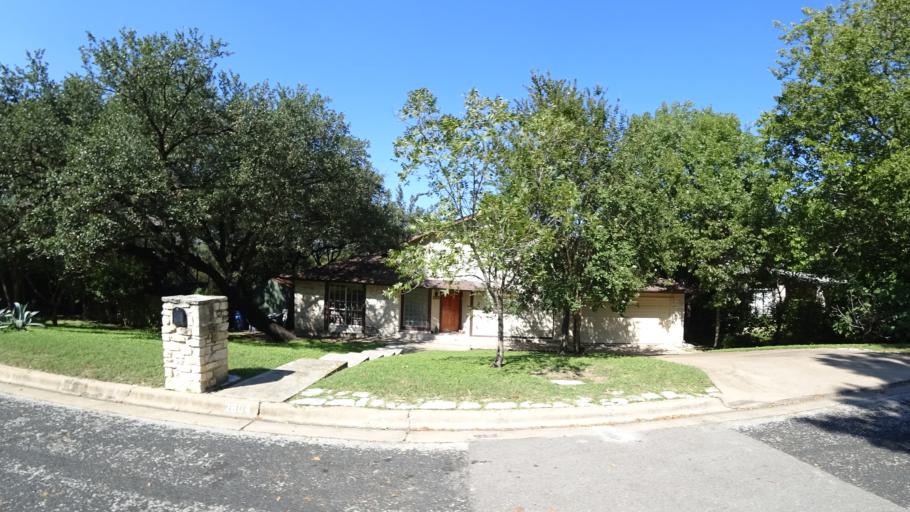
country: US
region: Texas
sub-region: Travis County
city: Rollingwood
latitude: 30.2519
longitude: -97.7861
